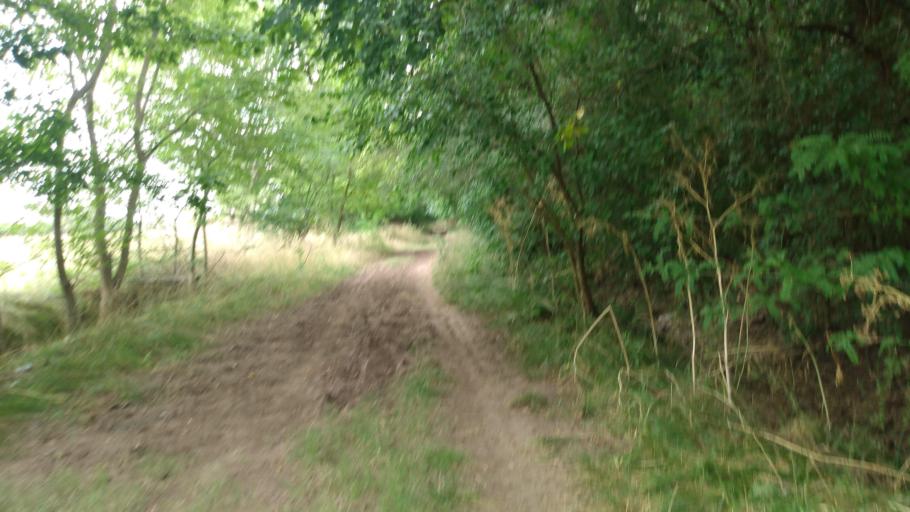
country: AR
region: Buenos Aires
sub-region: Partido de Lujan
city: Lujan
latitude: -34.5995
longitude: -59.0612
